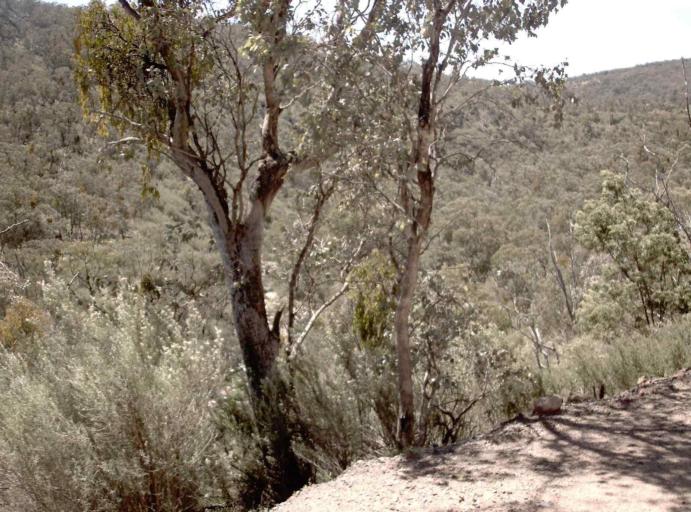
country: AU
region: New South Wales
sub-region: Snowy River
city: Jindabyne
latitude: -37.0419
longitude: 148.5380
